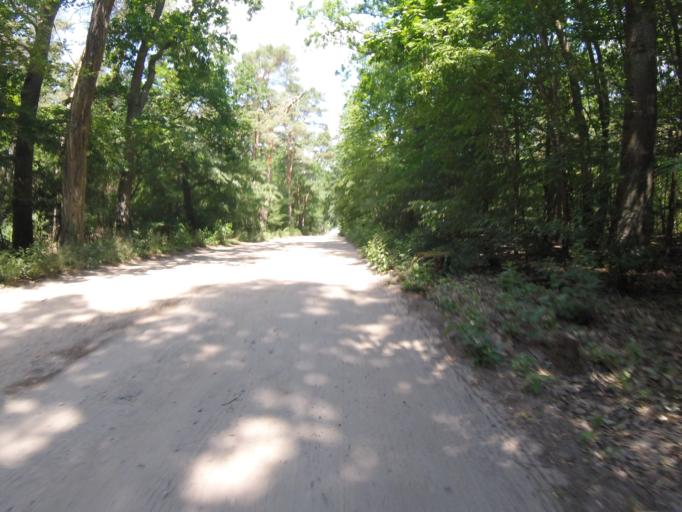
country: DE
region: Brandenburg
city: Bestensee
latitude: 52.2713
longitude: 13.6575
